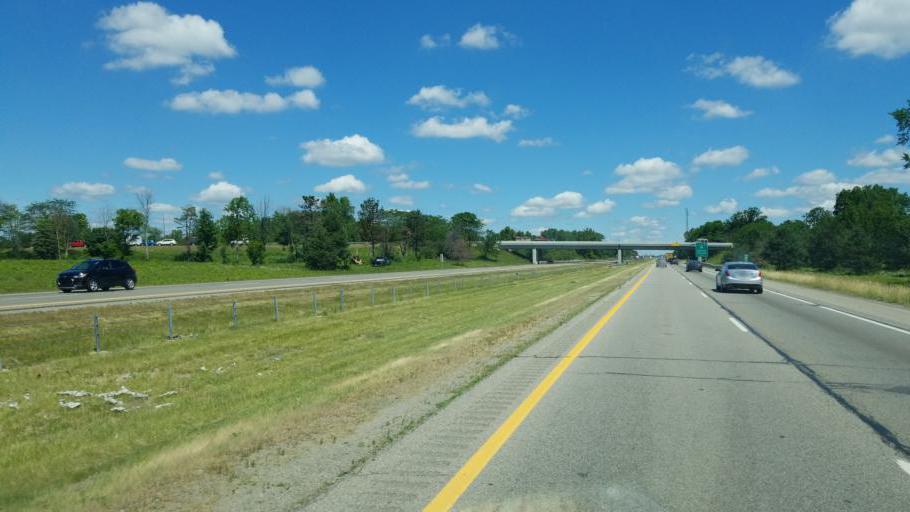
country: US
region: Michigan
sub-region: Washtenaw County
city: Ypsilanti
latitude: 42.2037
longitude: -83.6848
